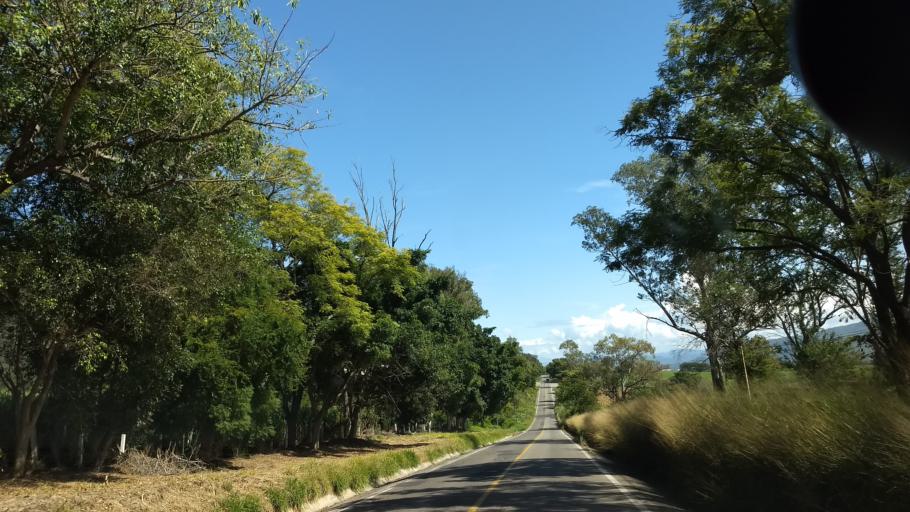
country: MX
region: Jalisco
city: Tuxpan
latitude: 19.5379
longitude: -103.4107
